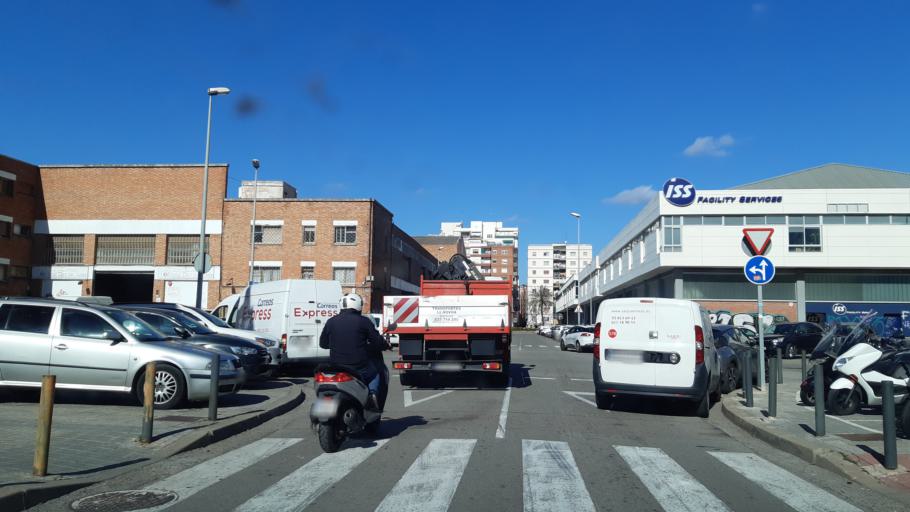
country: ES
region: Catalonia
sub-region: Provincia de Barcelona
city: L'Hospitalet de Llobregat
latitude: 41.3588
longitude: 2.1106
